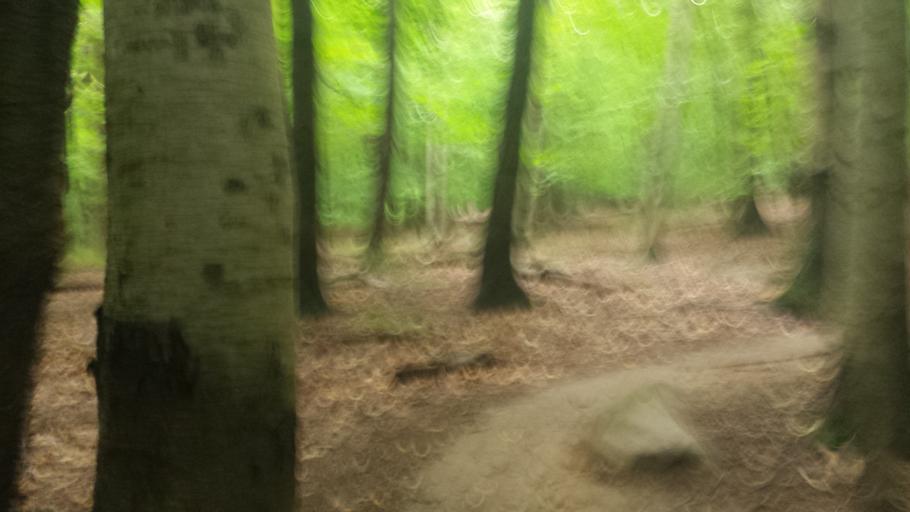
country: US
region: New York
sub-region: Westchester County
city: Hawthorne
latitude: 41.1187
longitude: -73.8010
